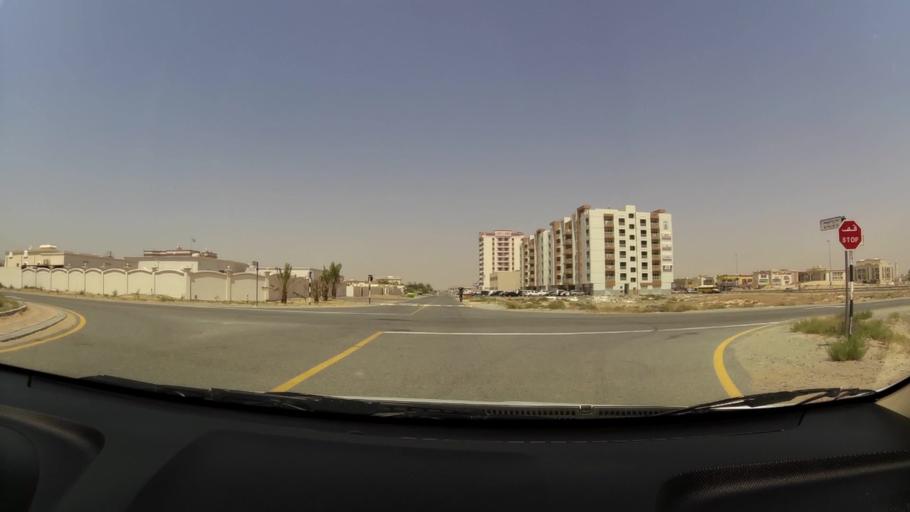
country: AE
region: Umm al Qaywayn
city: Umm al Qaywayn
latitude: 25.5064
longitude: 55.5875
